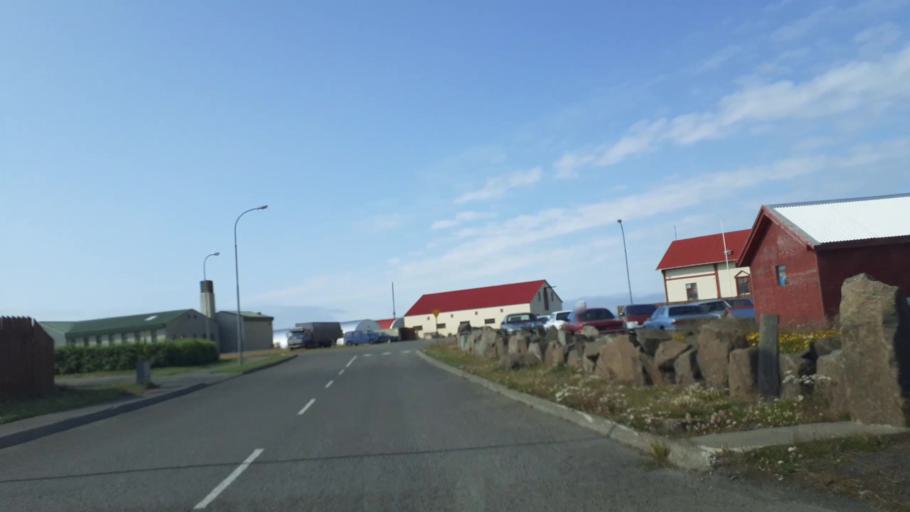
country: IS
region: Northwest
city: Saudarkrokur
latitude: 65.6648
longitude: -20.2911
